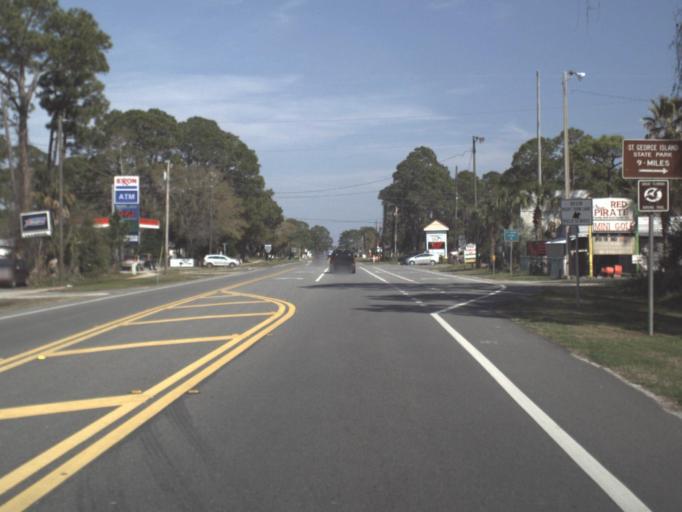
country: US
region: Florida
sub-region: Franklin County
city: Eastpoint
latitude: 29.7361
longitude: -84.8893
